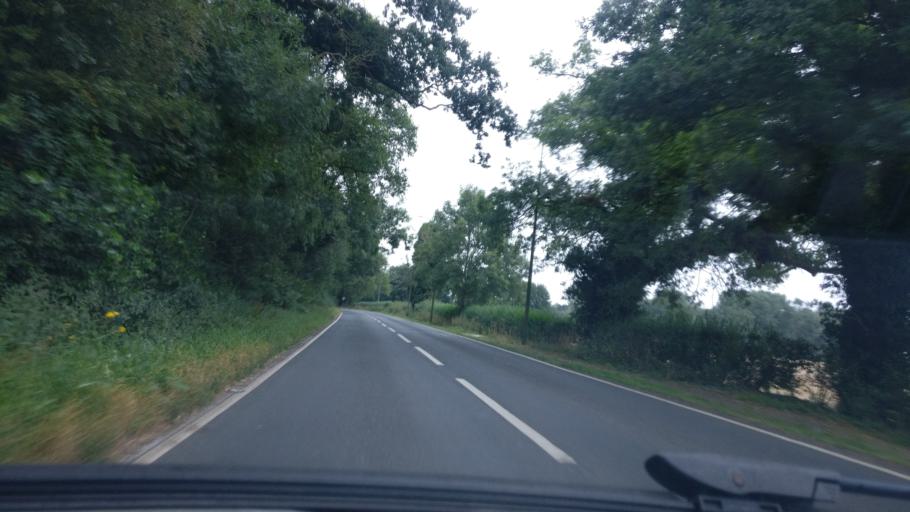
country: GB
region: England
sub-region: East Riding of Yorkshire
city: Leven
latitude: 53.8812
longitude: -0.3119
